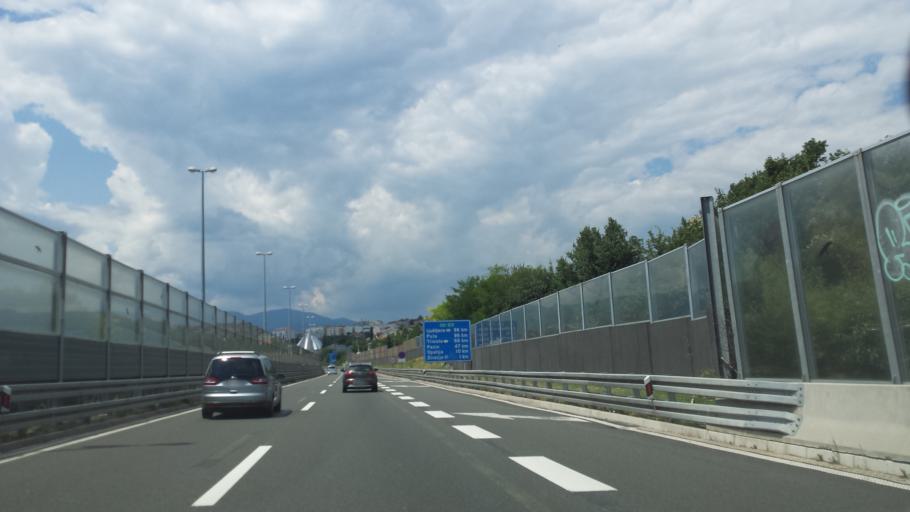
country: HR
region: Primorsko-Goranska
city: Rijeka
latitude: 45.3453
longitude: 14.3962
